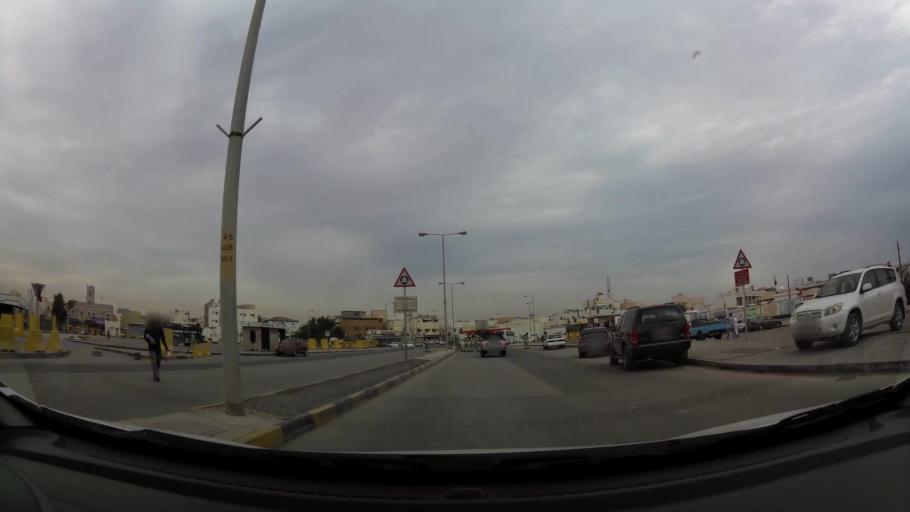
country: BH
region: Northern
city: Sitrah
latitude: 26.1605
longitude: 50.6175
